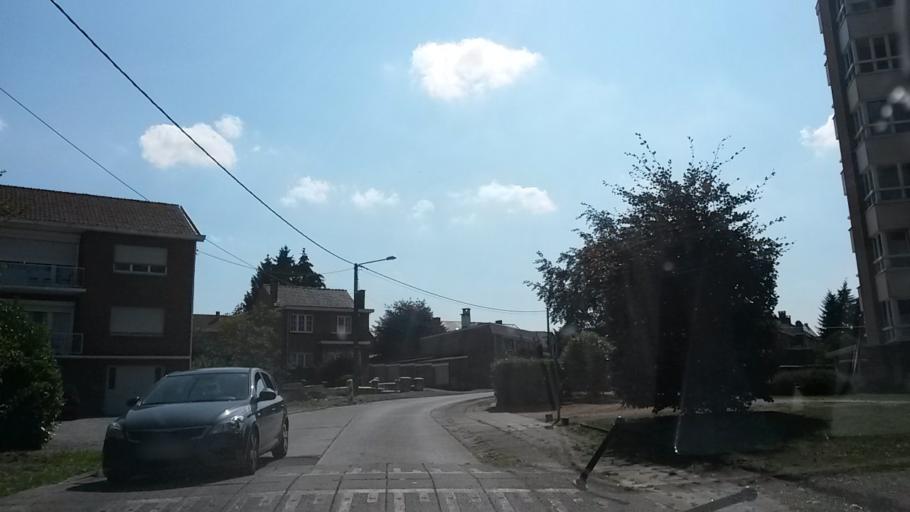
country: BE
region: Wallonia
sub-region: Province du Hainaut
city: Farciennes
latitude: 50.4337
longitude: 4.5051
